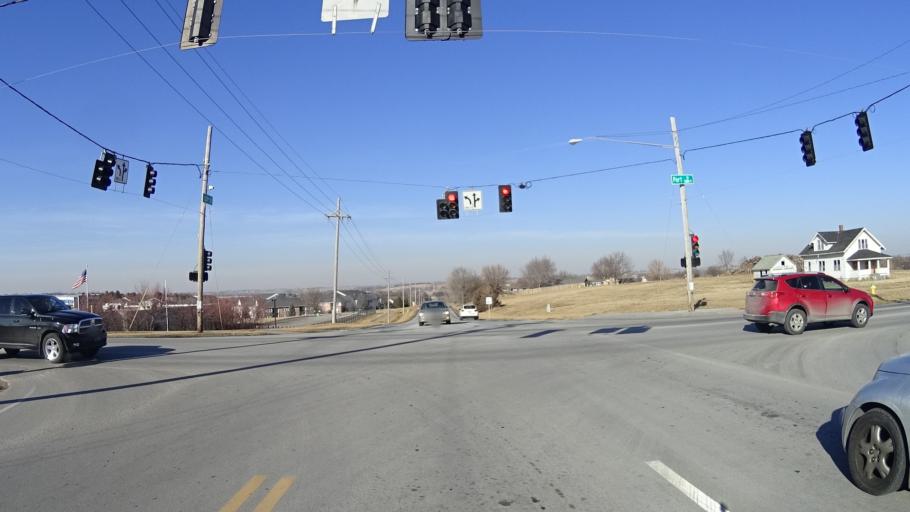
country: US
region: Nebraska
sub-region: Douglas County
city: Bennington
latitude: 41.3065
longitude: -96.1197
